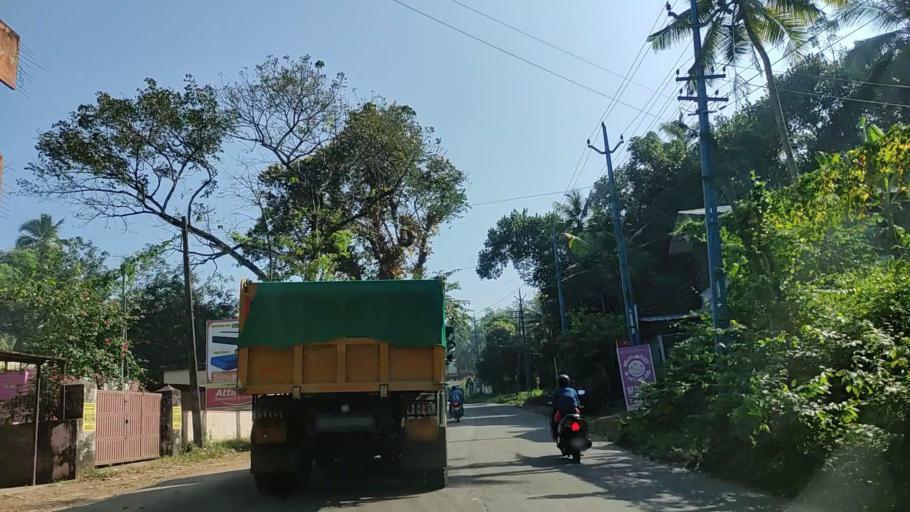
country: IN
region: Kerala
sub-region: Kollam
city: Punalur
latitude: 8.9168
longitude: 76.8918
